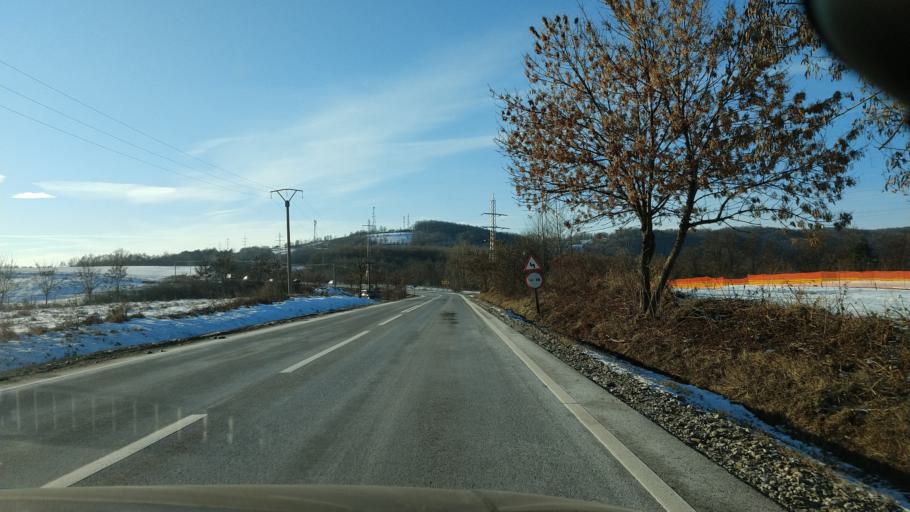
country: RO
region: Bacau
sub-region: Comuna Luizi-Calugara
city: Luizi-Calugara
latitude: 46.5084
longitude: 26.8179
